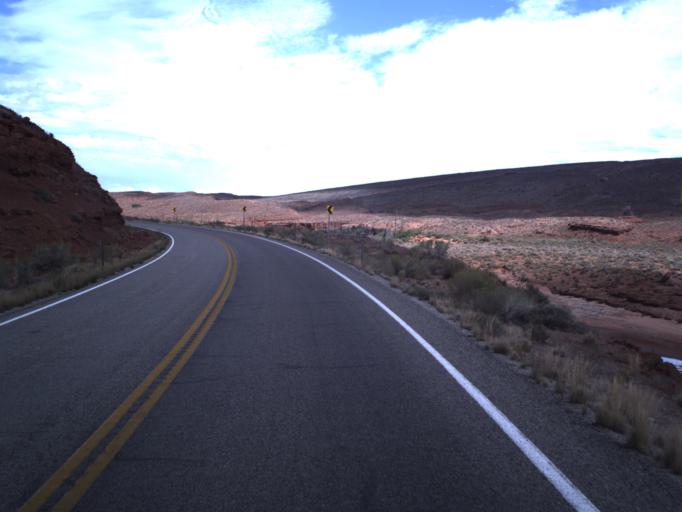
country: US
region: Utah
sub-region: San Juan County
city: Blanding
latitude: 37.2185
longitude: -109.8271
